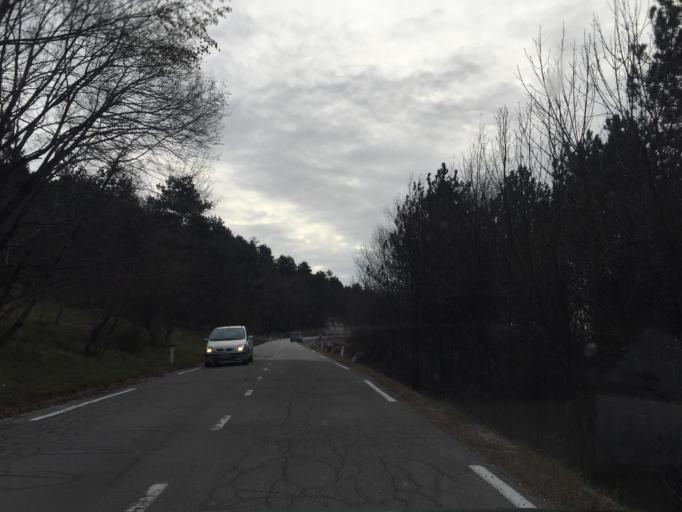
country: SI
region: Nova Gorica
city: Sempas
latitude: 45.9740
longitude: 13.7203
